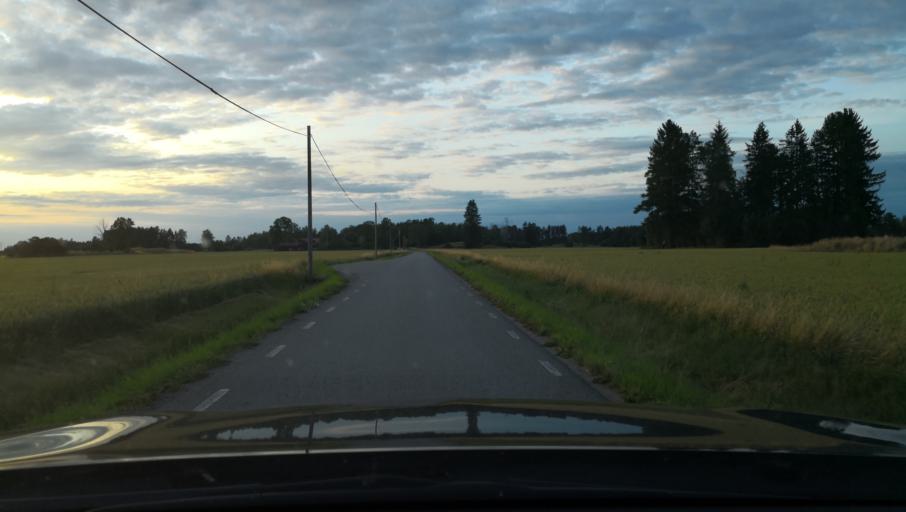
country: SE
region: Uppsala
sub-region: Uppsala Kommun
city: Vattholma
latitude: 60.0432
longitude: 17.6631
